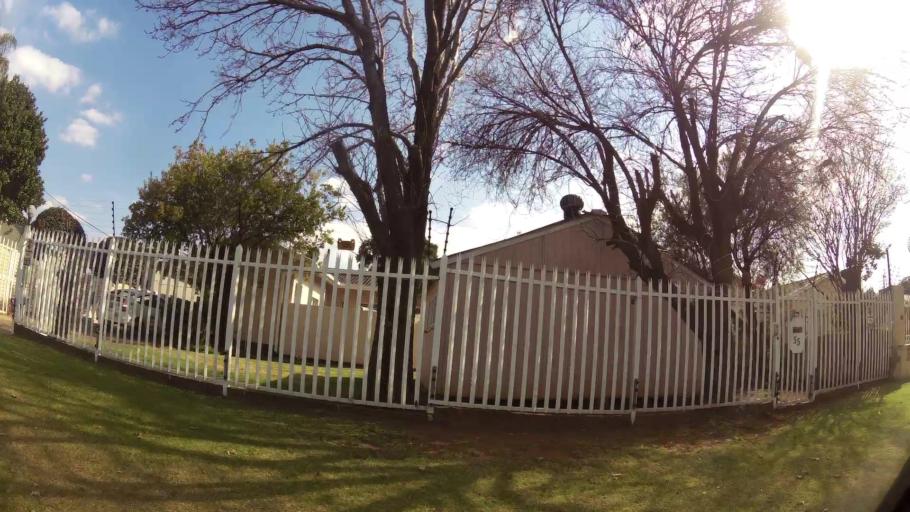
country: ZA
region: Gauteng
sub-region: Ekurhuleni Metropolitan Municipality
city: Germiston
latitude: -26.1789
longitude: 28.1990
